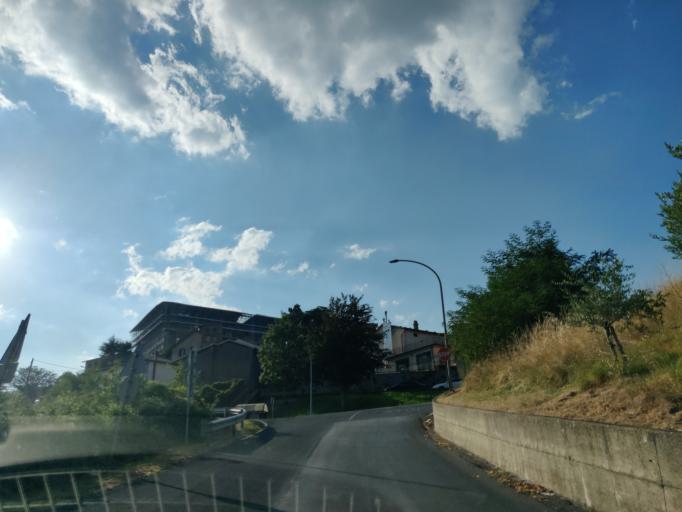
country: IT
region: Tuscany
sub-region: Provincia di Siena
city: Piancastagnaio
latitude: 42.8471
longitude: 11.6958
